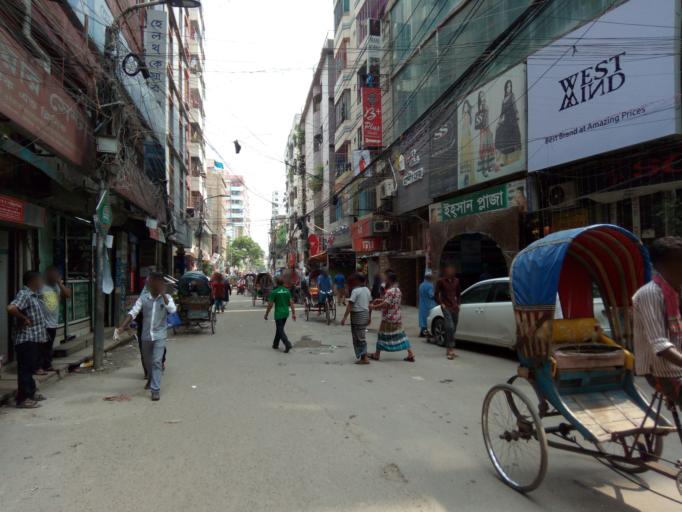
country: BD
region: Dhaka
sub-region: Dhaka
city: Dhaka
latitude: 23.7195
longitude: 90.4165
